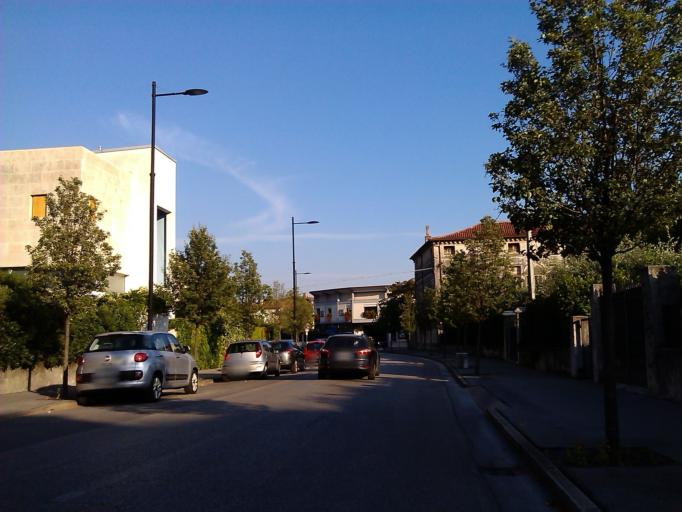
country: IT
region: Veneto
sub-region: Provincia di Vicenza
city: Bassano del Grappa
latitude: 45.7618
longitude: 11.7362
